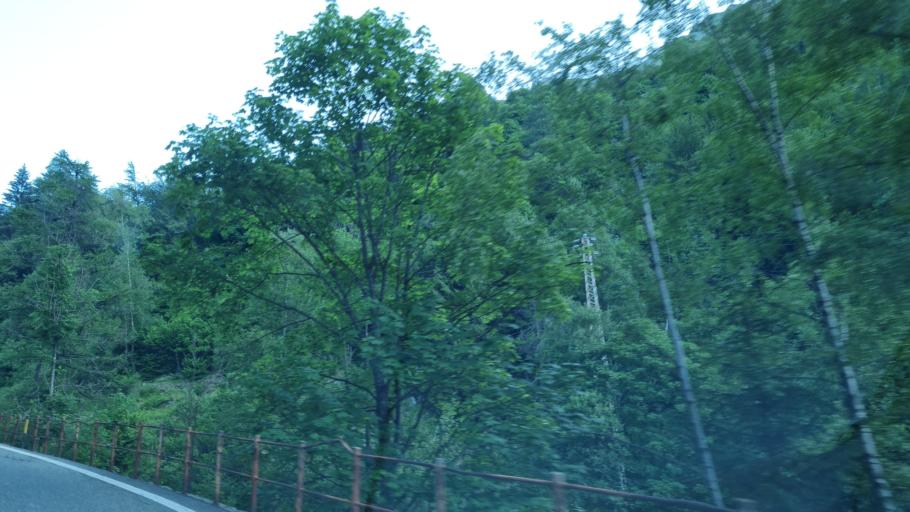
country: IT
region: Piedmont
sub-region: Provincia di Torino
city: Valprato Soana
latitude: 45.5377
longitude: 7.5379
